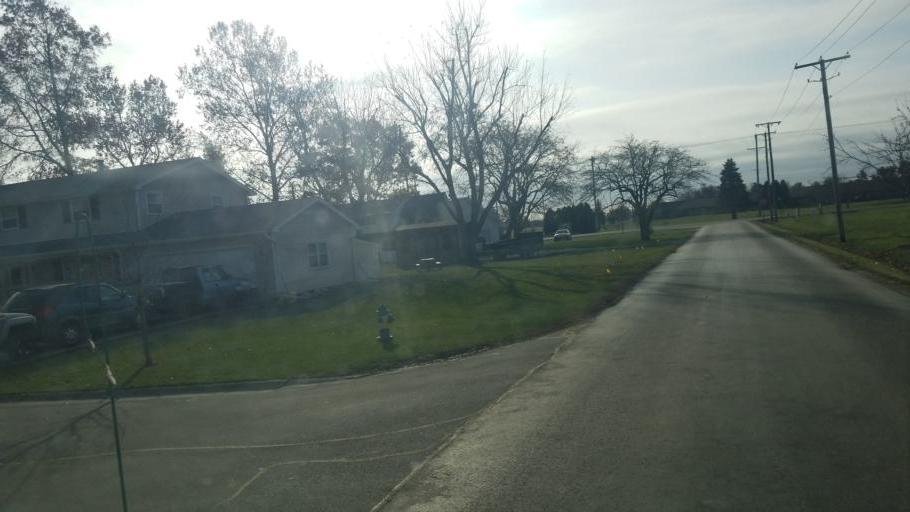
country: US
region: Indiana
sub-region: Adams County
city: Berne
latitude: 40.6584
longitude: -84.9652
